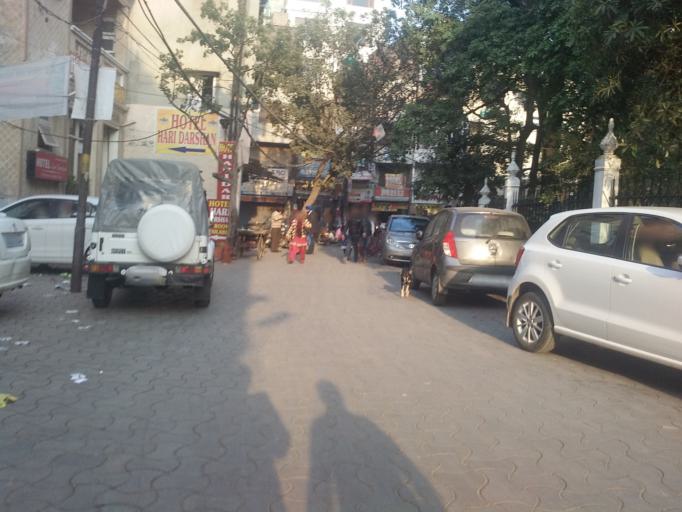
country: IN
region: Punjab
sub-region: Amritsar
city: Amritsar
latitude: 31.6214
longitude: 74.8755
